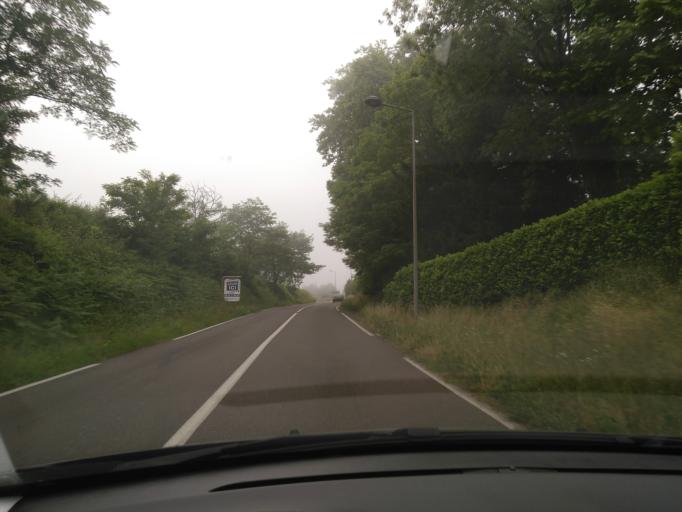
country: FR
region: Aquitaine
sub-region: Departement des Landes
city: Villeneuve-de-Marsan
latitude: 43.8899
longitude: -0.3942
